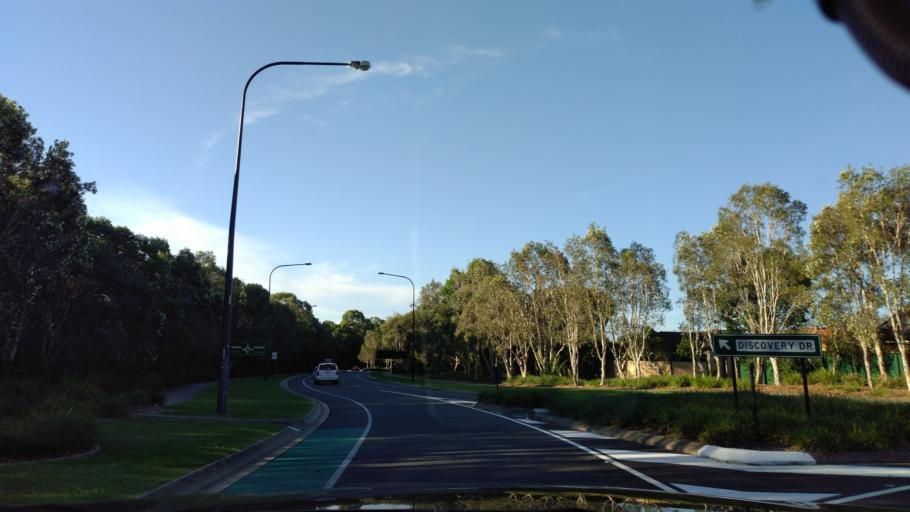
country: AU
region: Queensland
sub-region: Moreton Bay
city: Mango Hill
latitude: -27.2271
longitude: 153.0214
